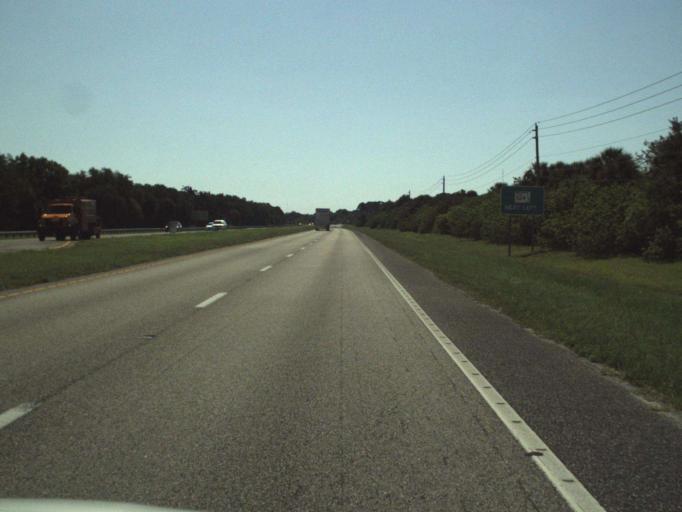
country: US
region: Florida
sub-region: Brevard County
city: Cocoa West
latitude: 28.3622
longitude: -80.8352
